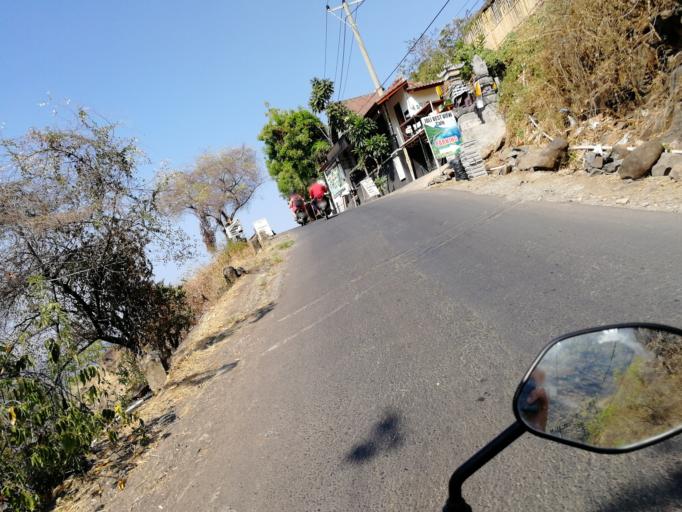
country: ID
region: Bali
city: Biaslantang Kaler
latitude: -8.3391
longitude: 115.6614
